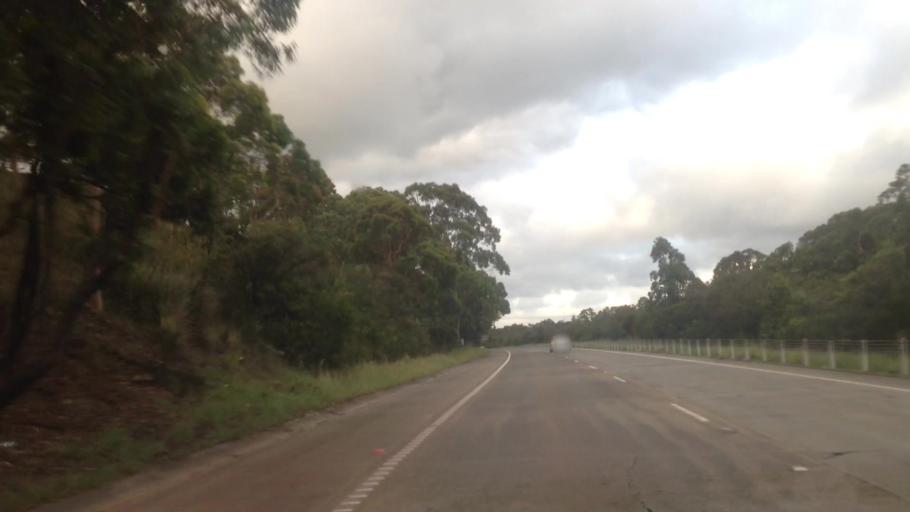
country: AU
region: New South Wales
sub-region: Wyong Shire
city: Charmhaven
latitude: -33.1993
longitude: 151.4629
